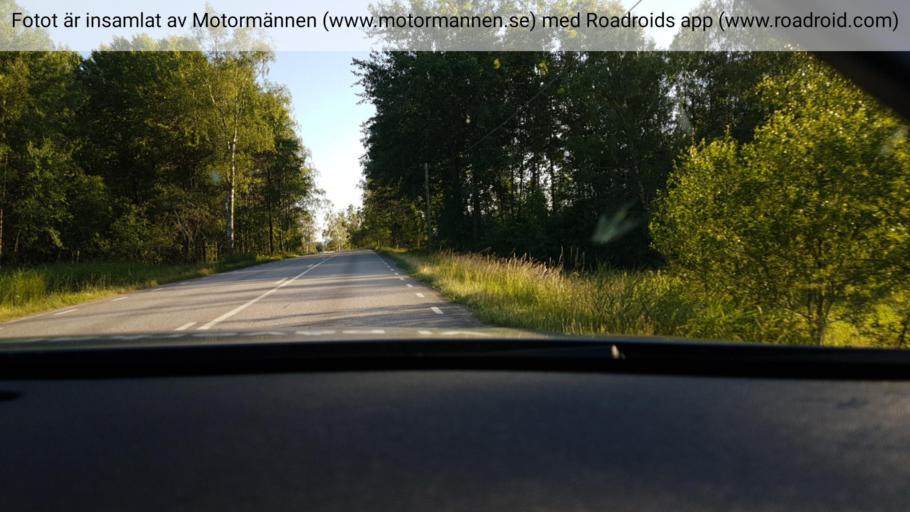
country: SE
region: Vaestra Goetaland
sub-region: Skovde Kommun
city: Stopen
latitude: 58.5224
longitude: 13.9818
